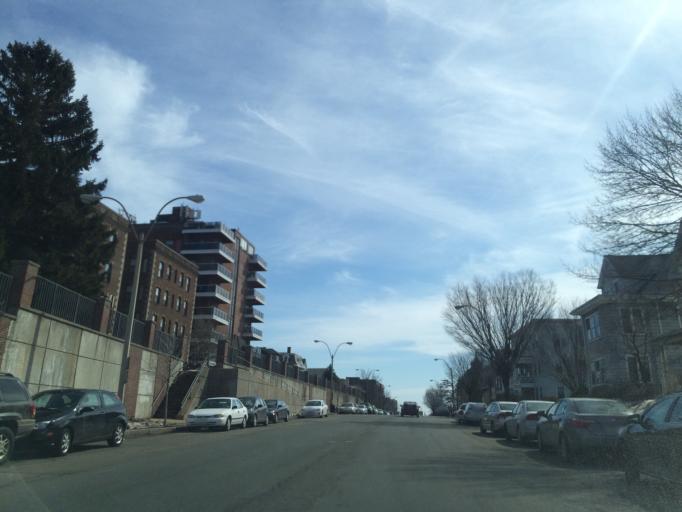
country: US
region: Massachusetts
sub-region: Middlesex County
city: Somerville
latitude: 42.3963
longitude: -71.1011
